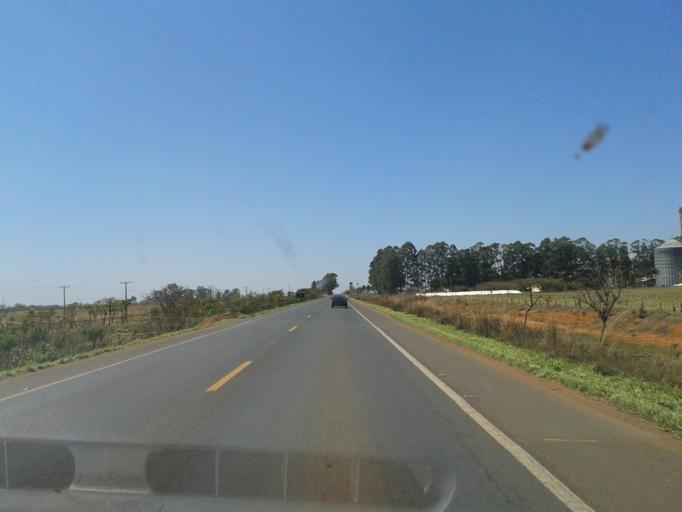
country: BR
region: Minas Gerais
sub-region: Uberaba
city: Uberaba
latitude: -19.3106
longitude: -47.5769
